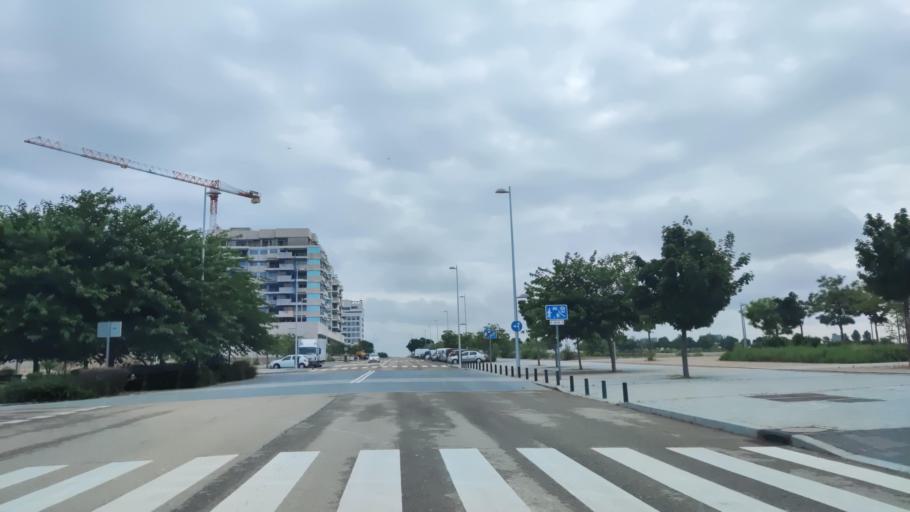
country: ES
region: Madrid
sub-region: Provincia de Madrid
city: Barajas de Madrid
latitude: 40.4887
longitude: -3.6066
